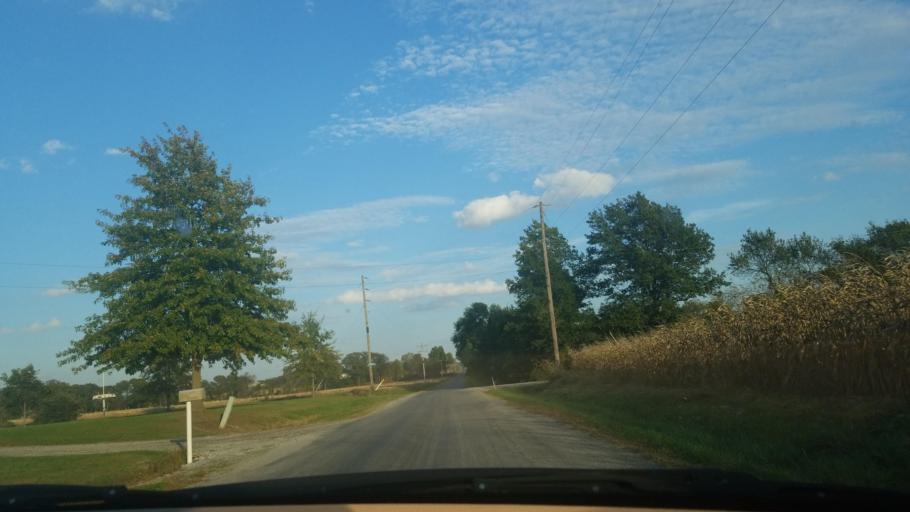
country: US
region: Illinois
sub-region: Saline County
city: Carrier Mills
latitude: 37.8050
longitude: -88.6755
